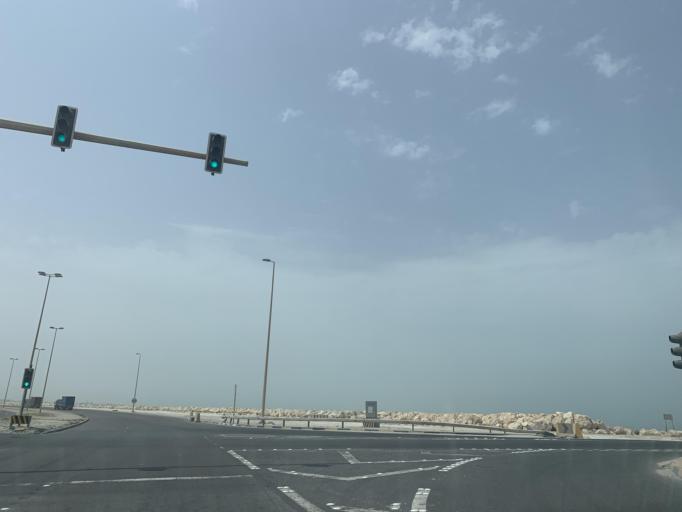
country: BH
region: Muharraq
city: Al Hadd
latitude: 26.2242
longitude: 50.6962
